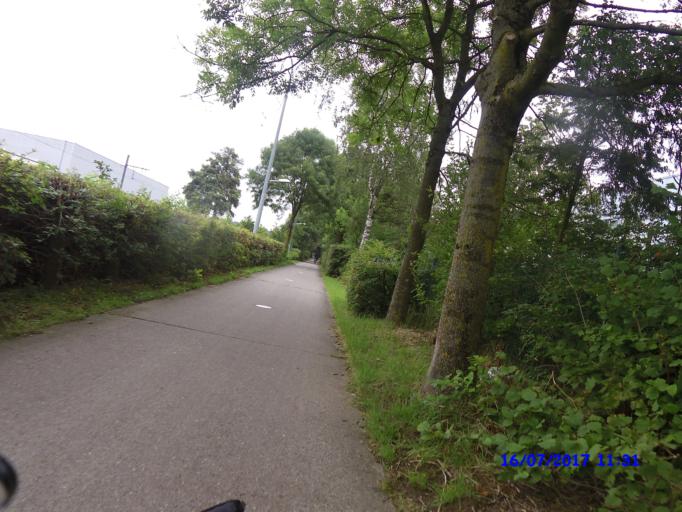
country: BE
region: Flanders
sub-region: Provincie Antwerpen
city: Turnhout
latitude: 51.3026
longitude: 4.9281
